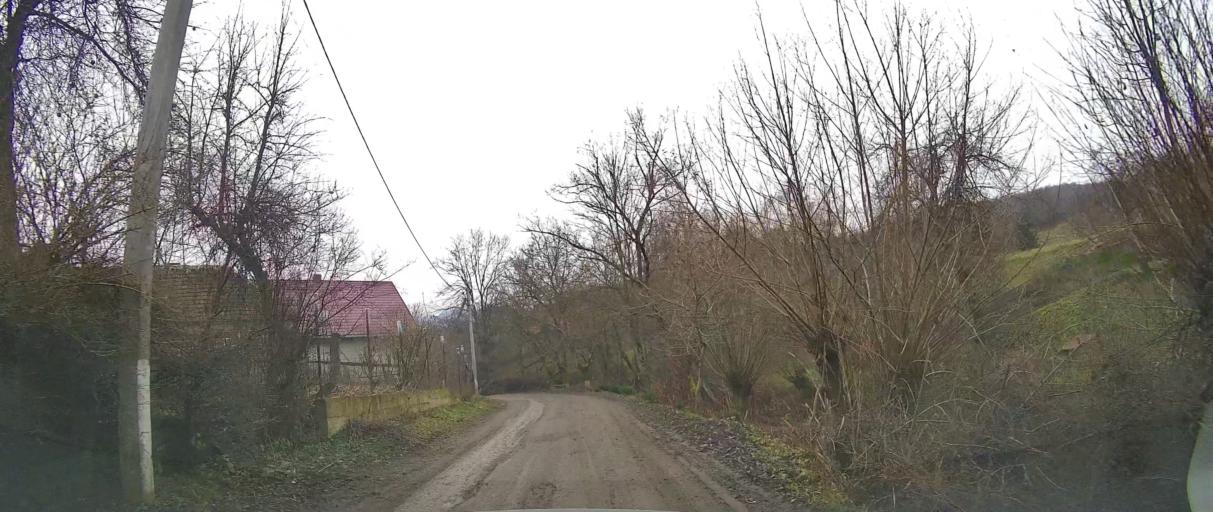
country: UA
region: Zakarpattia
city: Velykyi Bereznyi
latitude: 48.9716
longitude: 22.5494
